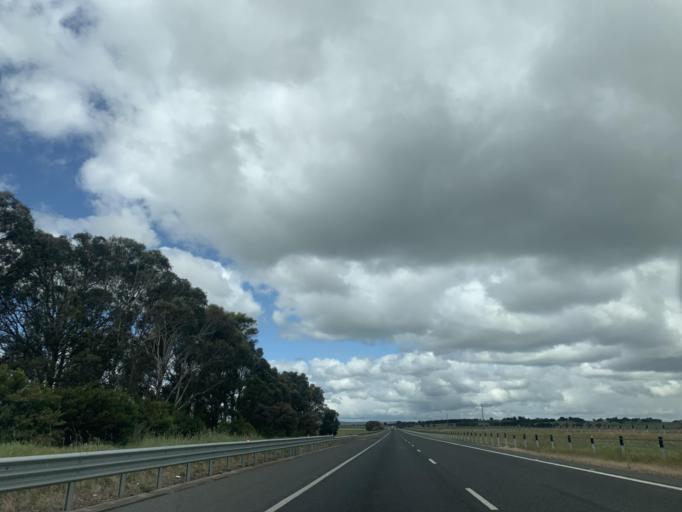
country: AU
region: Victoria
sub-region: Ballarat North
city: Newington
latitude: -37.4820
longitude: 143.7320
